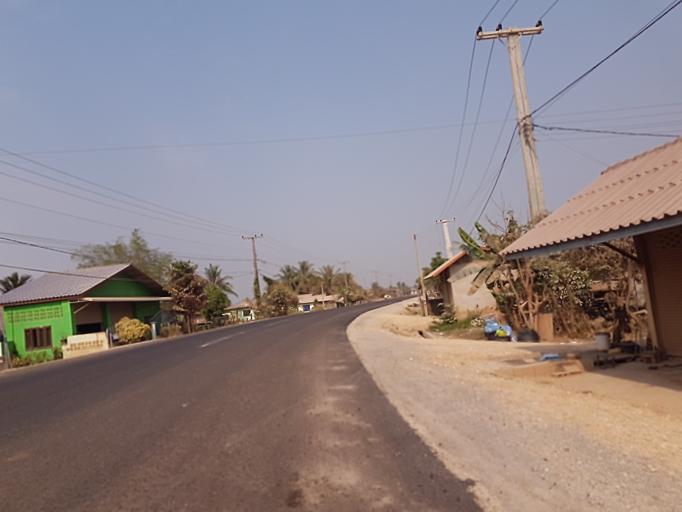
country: TH
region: Nong Khai
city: Nong Khai
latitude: 17.9270
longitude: 102.7706
